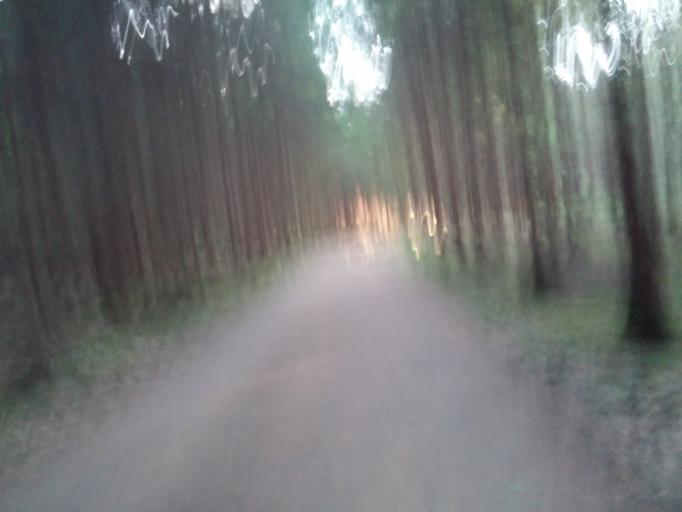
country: DE
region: Bavaria
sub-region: Upper Bavaria
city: Zorneding
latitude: 48.1185
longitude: 11.8153
